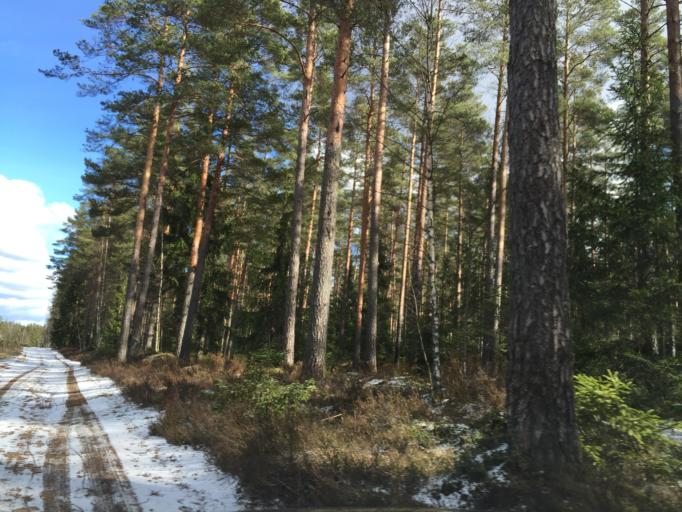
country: LV
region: Garkalne
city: Garkalne
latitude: 56.9687
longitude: 24.4277
